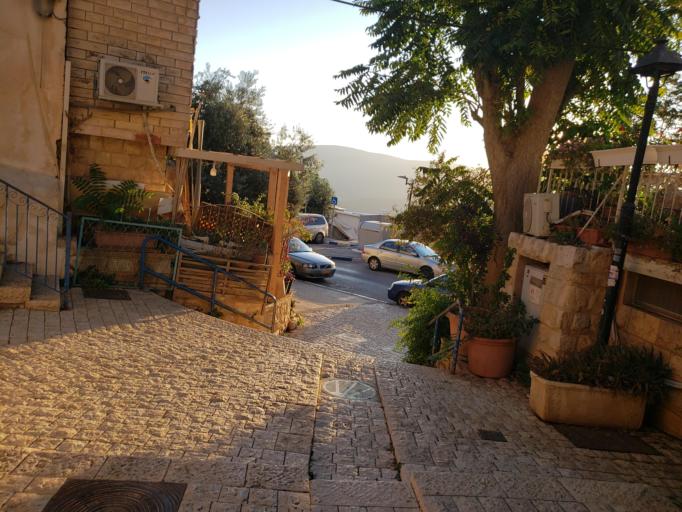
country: IL
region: Northern District
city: Safed
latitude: 32.9708
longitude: 35.4929
